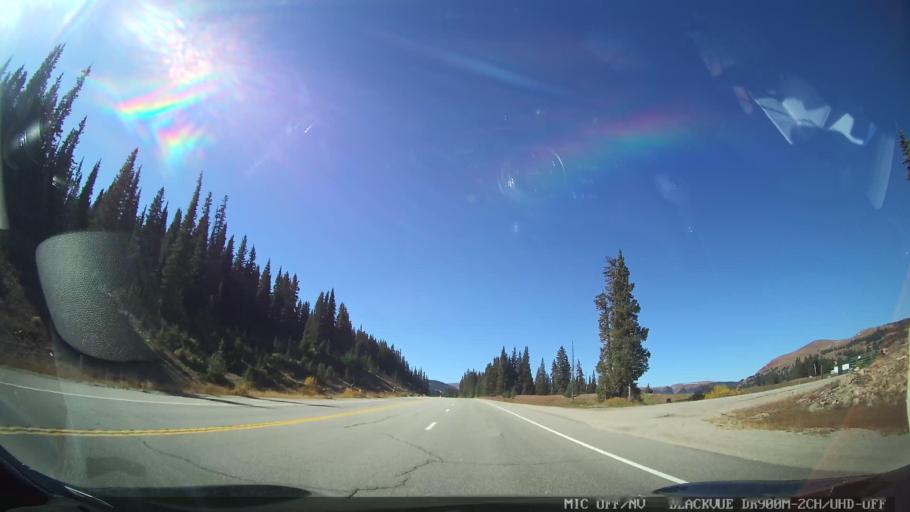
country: US
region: Colorado
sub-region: Summit County
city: Breckenridge
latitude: 39.4117
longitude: -106.1785
